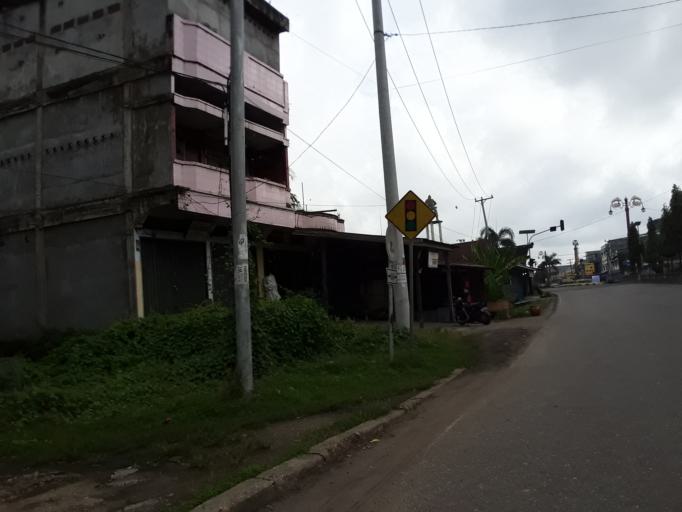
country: ID
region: Jambi
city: Muara Bulian
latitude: -1.7117
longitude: 103.2560
